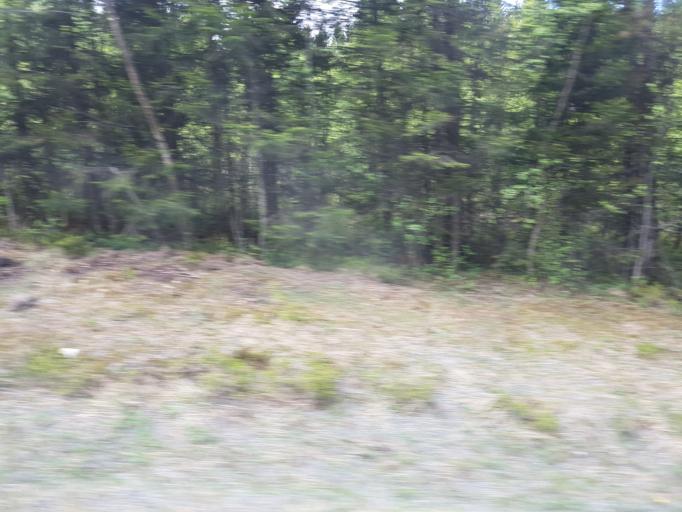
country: NO
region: Nord-Trondelag
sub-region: Levanger
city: Skogn
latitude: 63.6526
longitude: 11.2401
